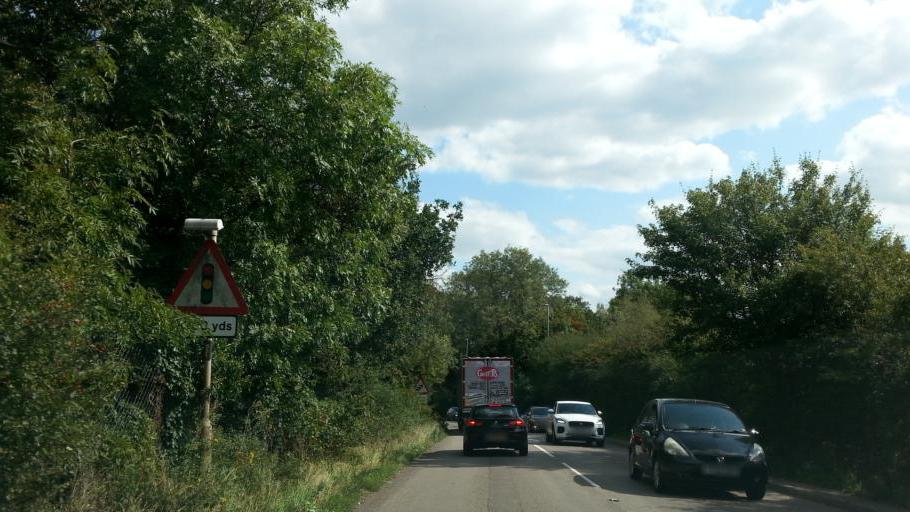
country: GB
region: England
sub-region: Leicestershire
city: Kirby Muxloe
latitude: 52.6311
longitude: -1.2112
